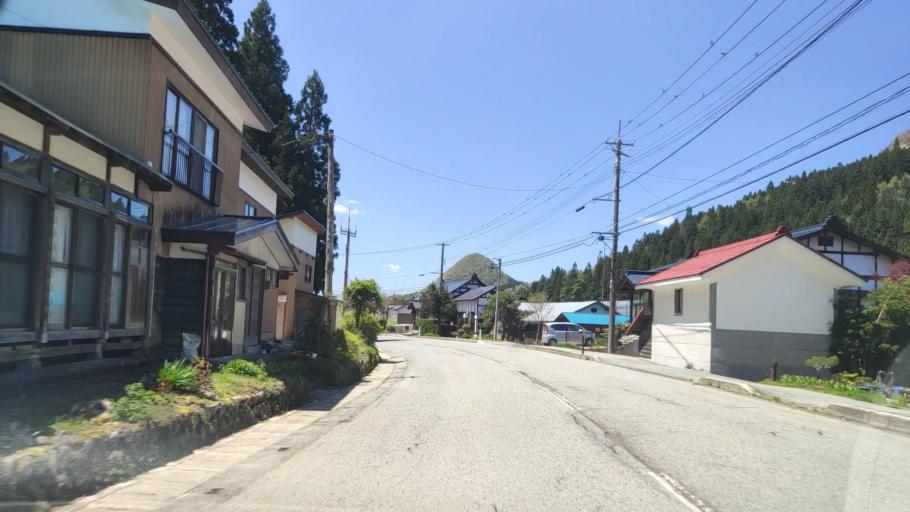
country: JP
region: Yamagata
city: Shinjo
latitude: 38.9231
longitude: 140.3356
